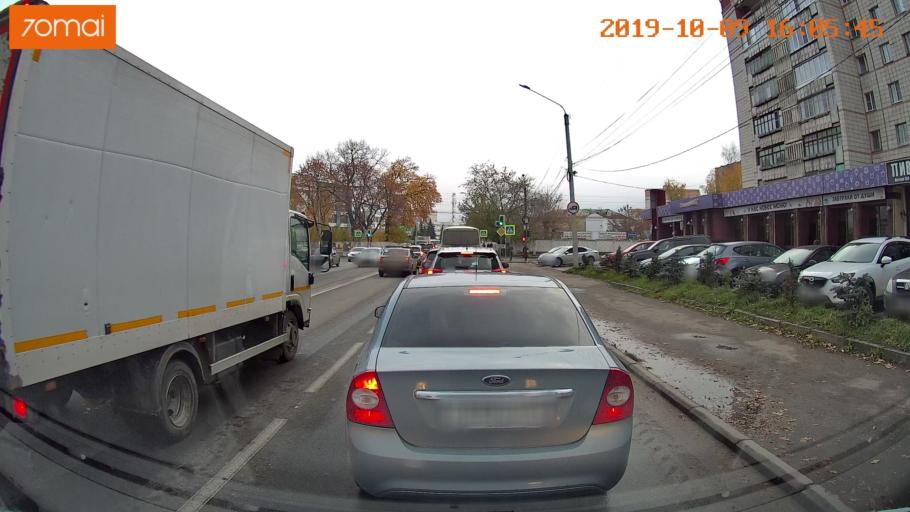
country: RU
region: Kostroma
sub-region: Kostromskoy Rayon
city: Kostroma
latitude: 57.7641
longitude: 40.9513
